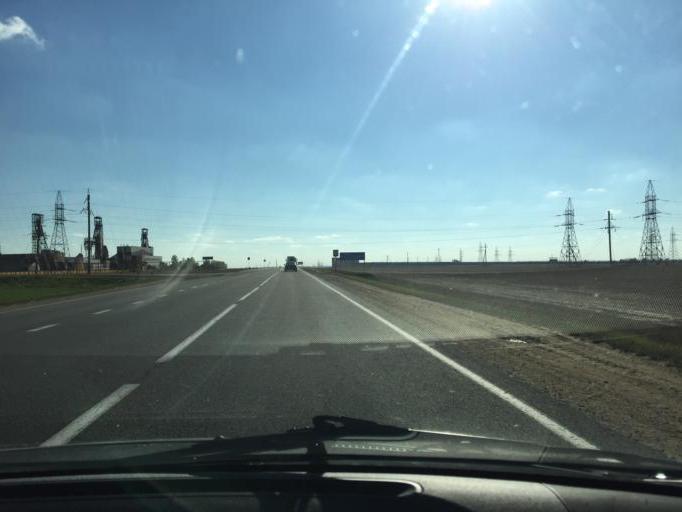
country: BY
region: Minsk
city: Salihorsk
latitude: 52.8625
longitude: 27.4669
